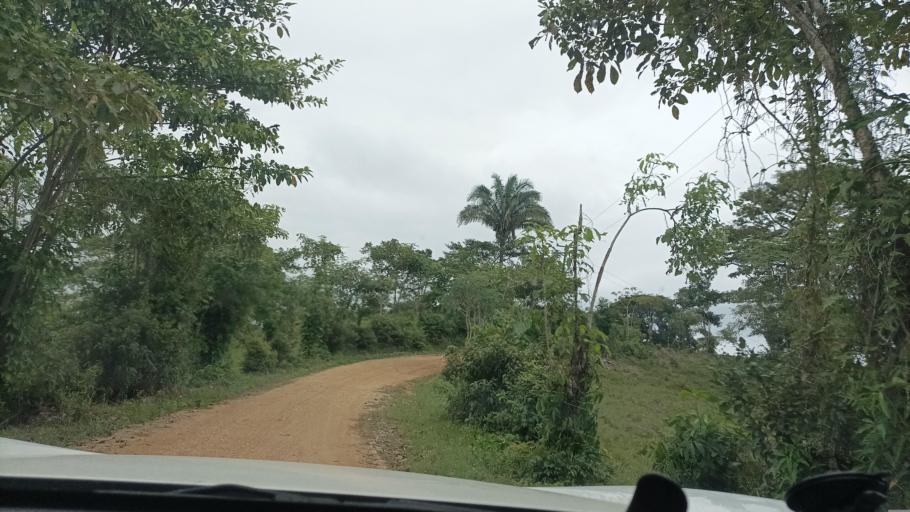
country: MX
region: Veracruz
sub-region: Uxpanapa
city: Poblado Cinco
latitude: 17.4896
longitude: -94.5721
